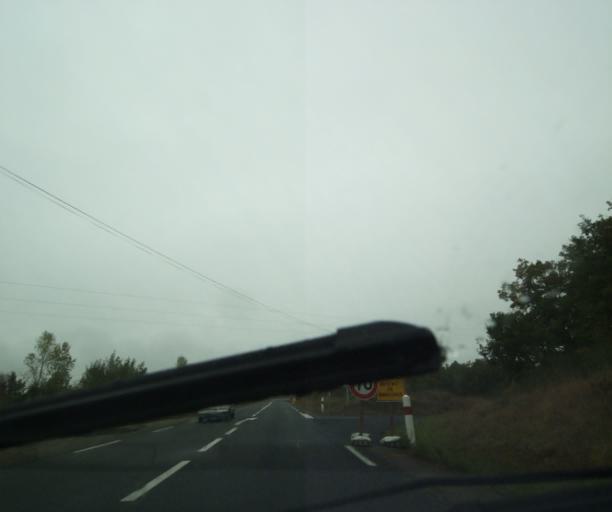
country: FR
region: Midi-Pyrenees
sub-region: Departement de l'Aveyron
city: Millau
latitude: 44.0825
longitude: 3.1247
